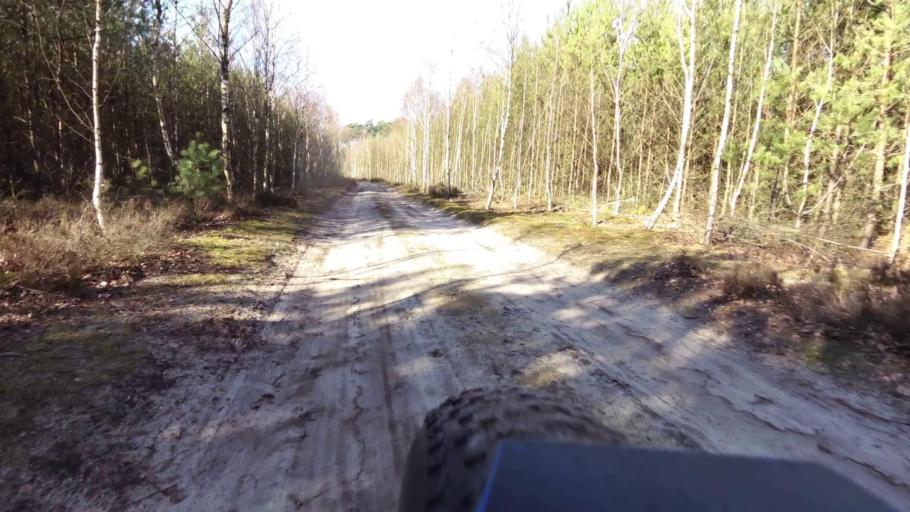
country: PL
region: Lubusz
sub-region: Powiat sulecinski
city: Torzym
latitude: 52.2194
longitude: 14.9976
